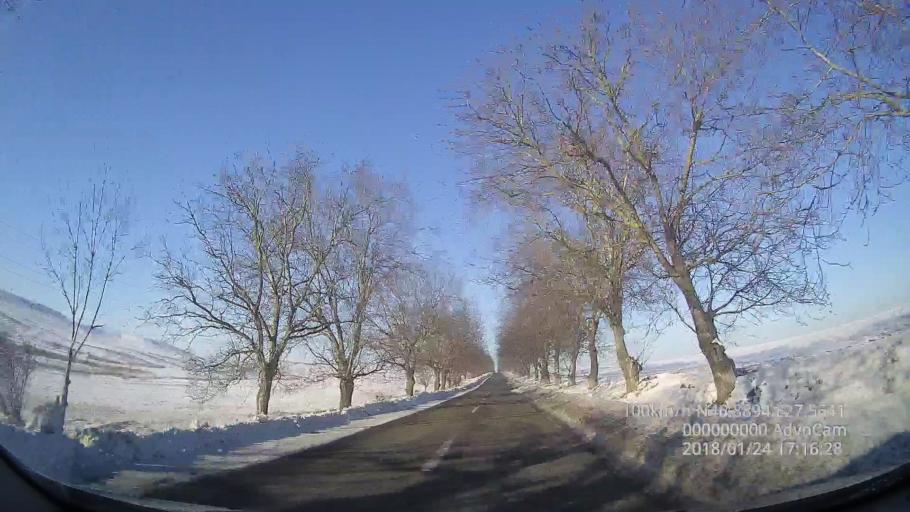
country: RO
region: Iasi
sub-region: Comuna Scanteia
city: Scanteia
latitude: 46.8902
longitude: 27.5641
